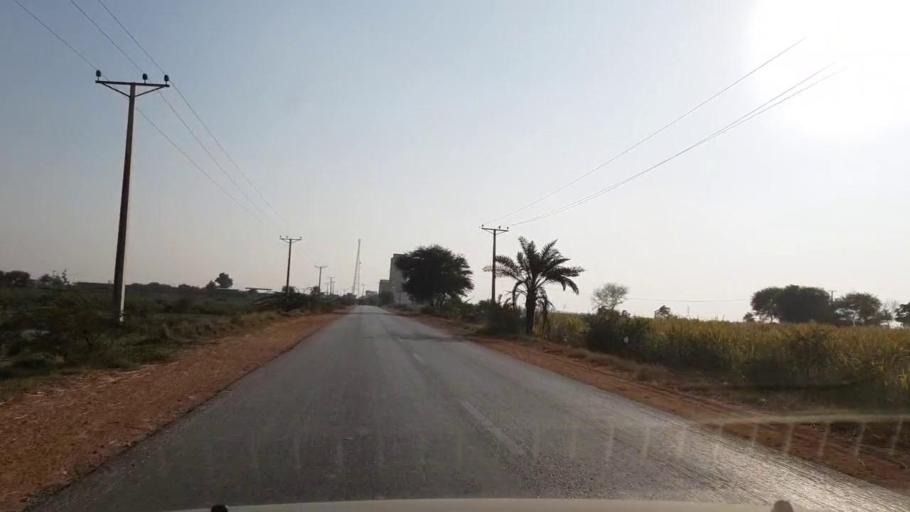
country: PK
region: Sindh
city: Bulri
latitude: 24.8340
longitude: 68.3235
